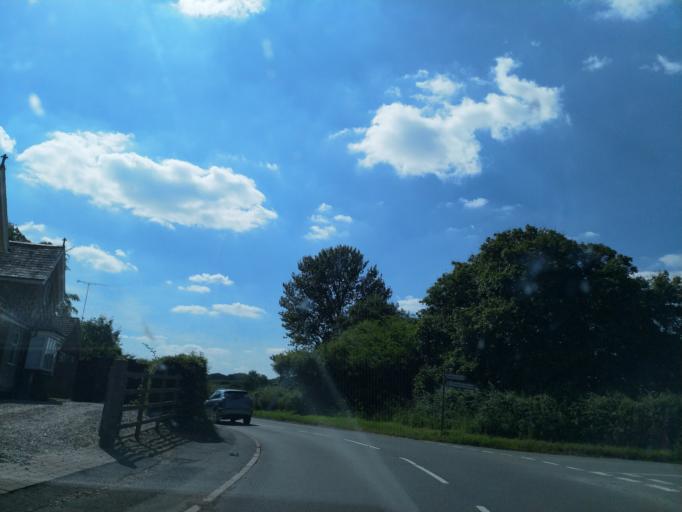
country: GB
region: England
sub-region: Warwickshire
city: Warwick
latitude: 52.2846
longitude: -1.6225
